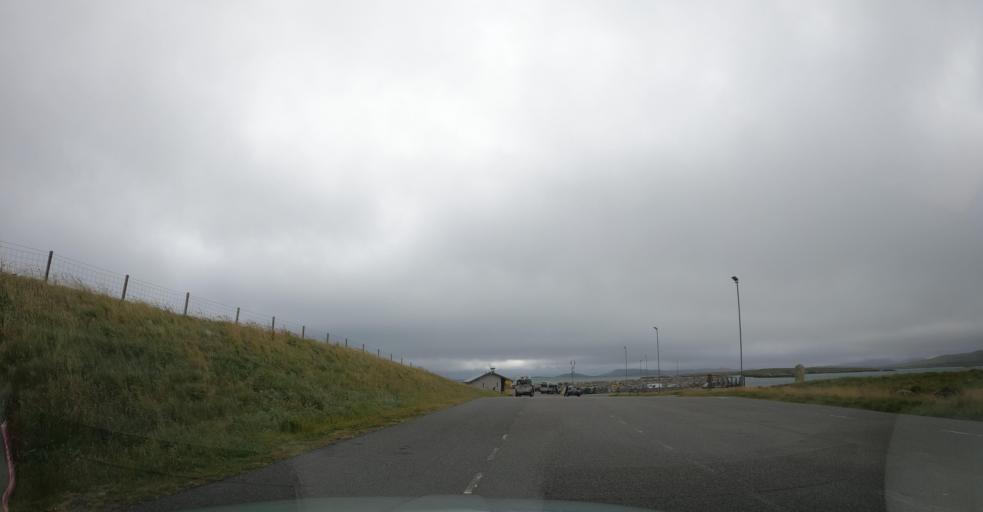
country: GB
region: Scotland
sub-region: Eilean Siar
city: Isle of North Uist
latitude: 57.7035
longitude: -7.1813
